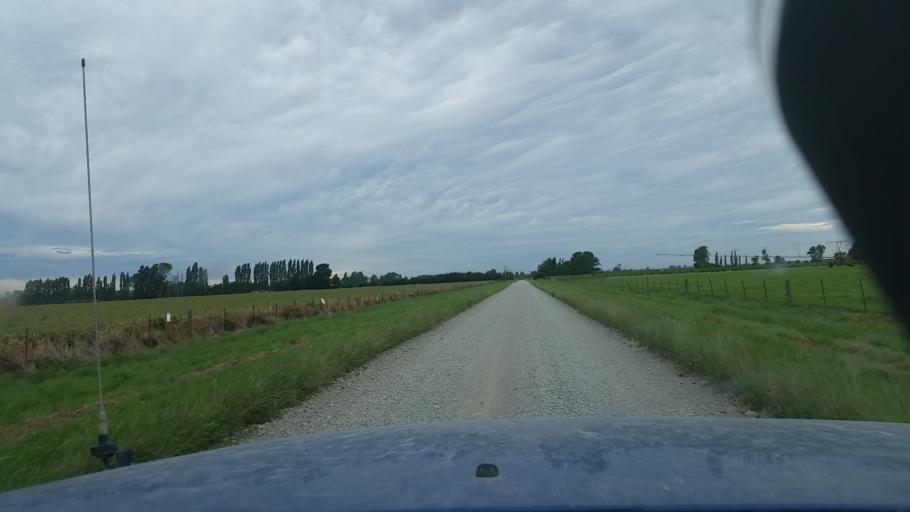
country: NZ
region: Canterbury
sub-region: Ashburton District
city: Ashburton
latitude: -43.8206
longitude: 171.6359
